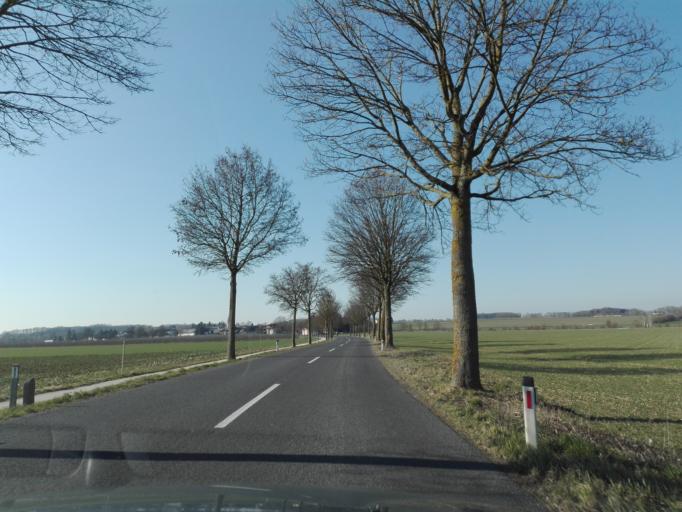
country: AT
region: Upper Austria
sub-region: Politischer Bezirk Linz-Land
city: Horsching
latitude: 48.2305
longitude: 14.1455
